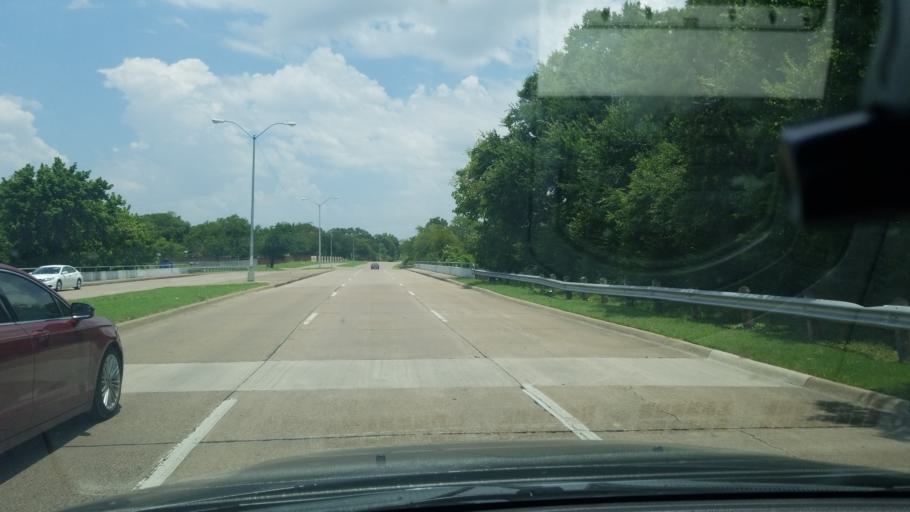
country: US
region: Texas
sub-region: Dallas County
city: Balch Springs
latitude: 32.7237
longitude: -96.6660
